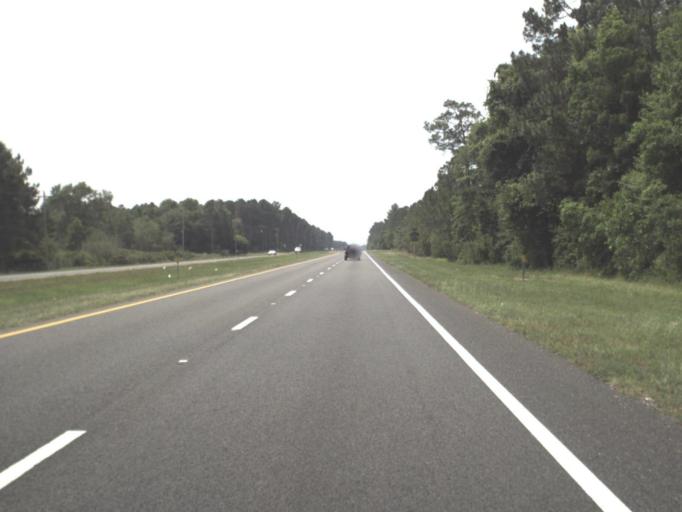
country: US
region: Florida
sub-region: Clay County
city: Green Cove Springs
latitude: 29.8572
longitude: -81.6631
